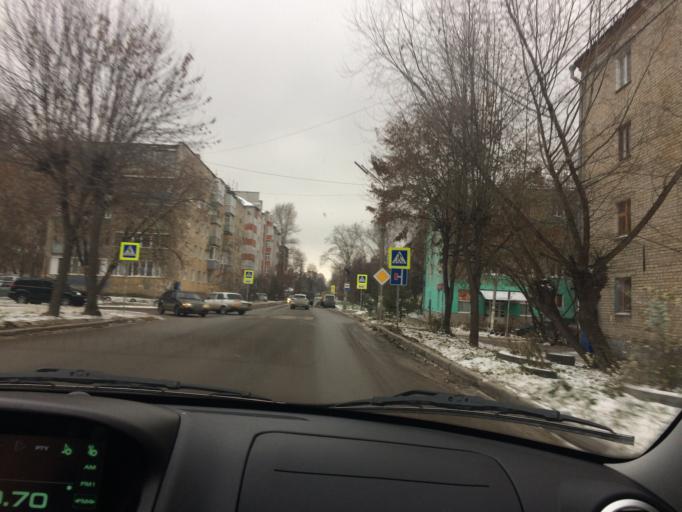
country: RU
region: Rjazan
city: Ryazan'
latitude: 54.6193
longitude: 39.7187
